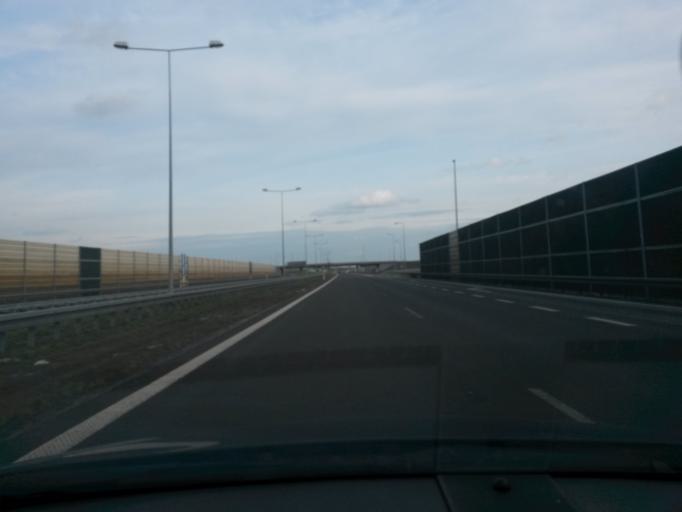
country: PL
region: Greater Poland Voivodeship
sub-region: Powiat kolski
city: Dabie
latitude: 52.0725
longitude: 18.8113
